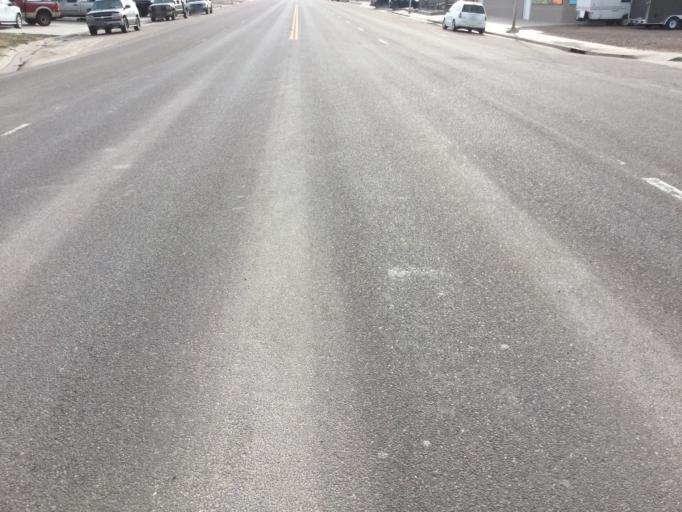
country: US
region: Kansas
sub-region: Scott County
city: Scott City
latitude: 38.4825
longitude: -100.9122
